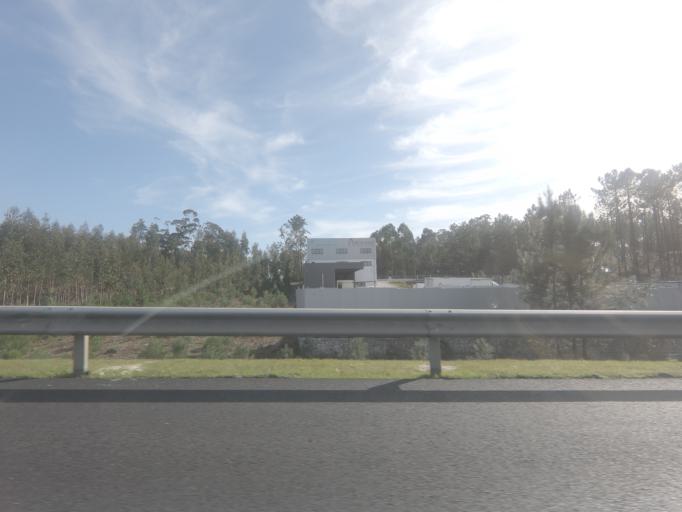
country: PT
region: Leiria
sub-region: Leiria
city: Caranguejeira
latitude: 39.7368
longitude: -8.7491
